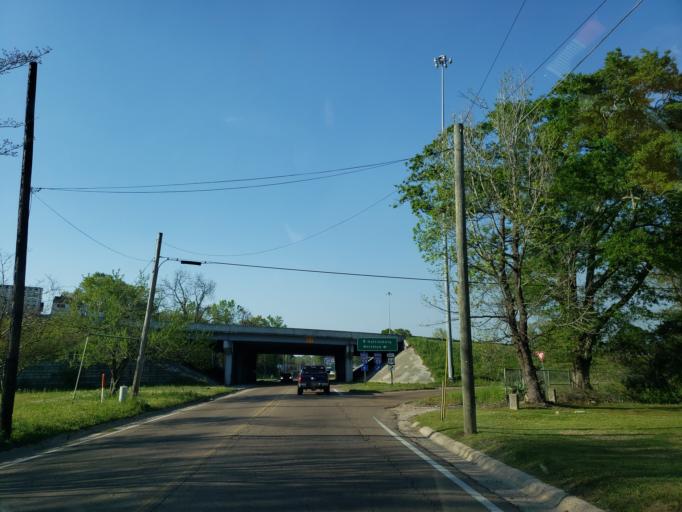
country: US
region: Mississippi
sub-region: Jones County
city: Laurel
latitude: 31.6868
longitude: -89.1231
